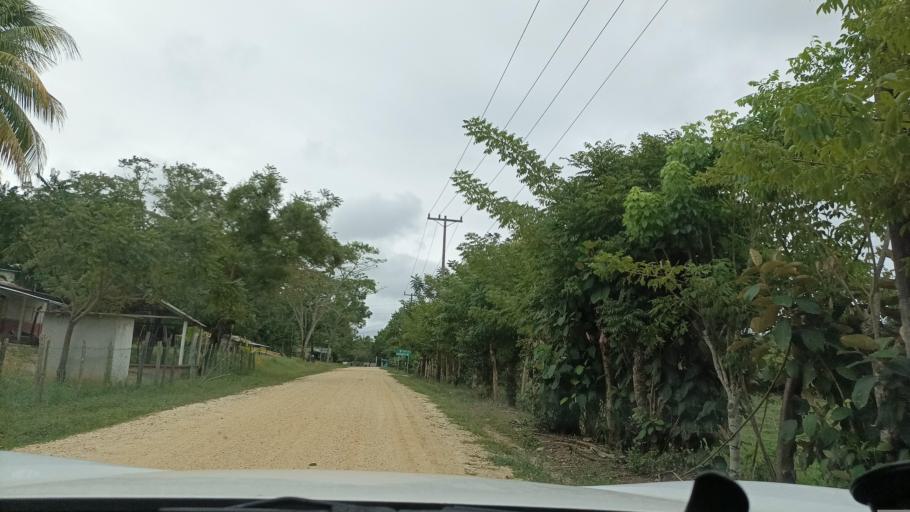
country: MX
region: Veracruz
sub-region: Moloacan
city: Cuichapa
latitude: 17.8537
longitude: -94.3572
